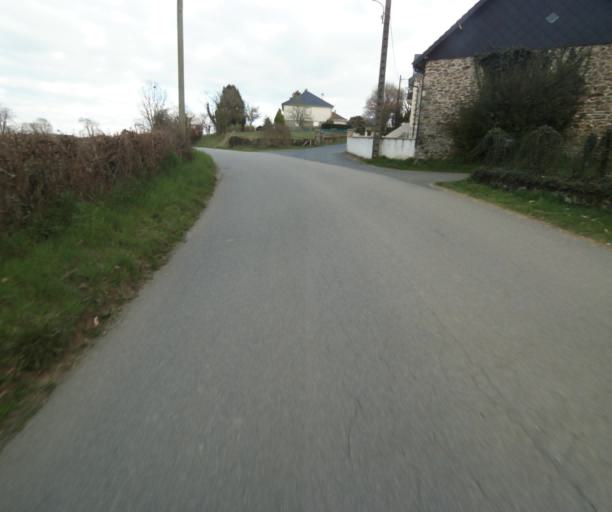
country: FR
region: Limousin
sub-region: Departement de la Correze
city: Saint-Clement
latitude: 45.3549
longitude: 1.6335
